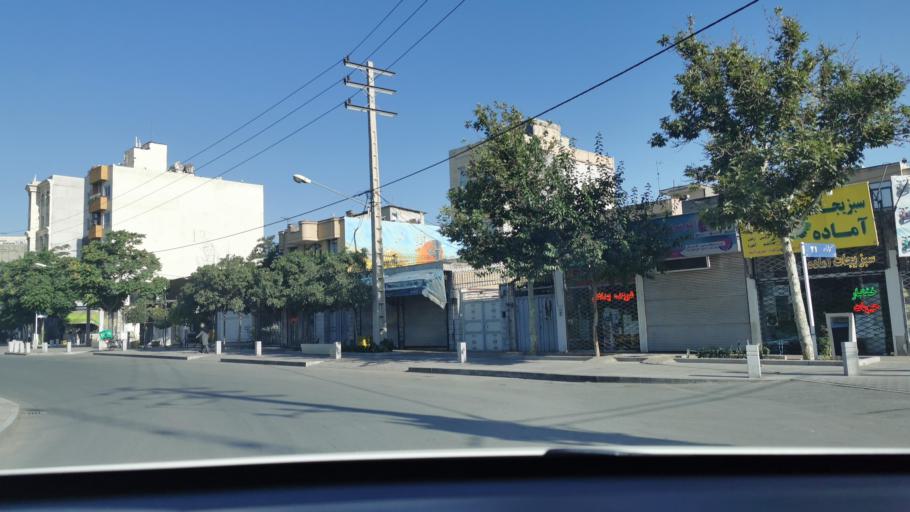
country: IR
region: Razavi Khorasan
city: Mashhad
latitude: 36.3118
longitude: 59.5126
